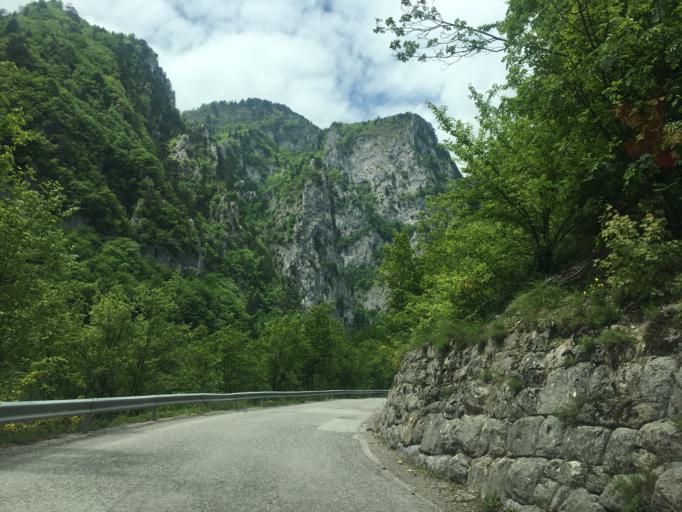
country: XK
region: Pec
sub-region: Komuna e Pejes
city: Peje
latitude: 42.6629
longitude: 20.2157
